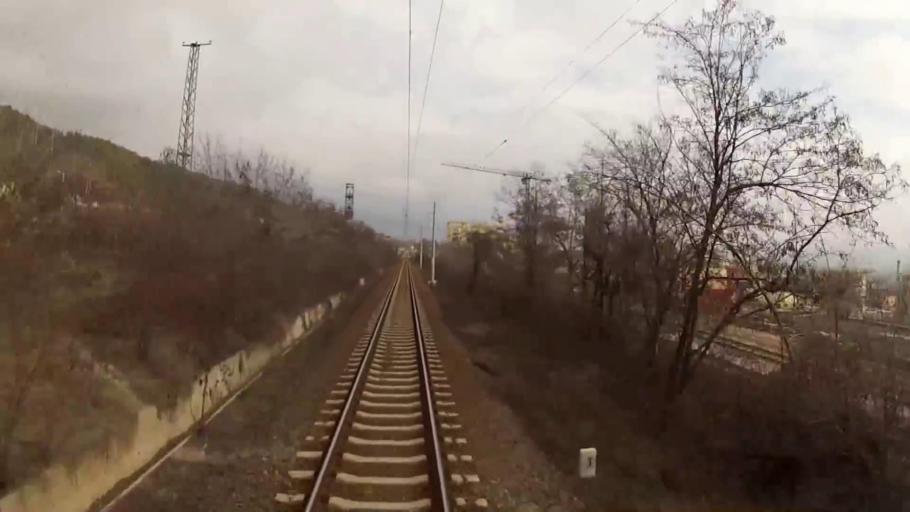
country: BG
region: Sofiya
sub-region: Obshtina Chelopech
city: Chelopech
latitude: 42.6946
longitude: 24.0705
